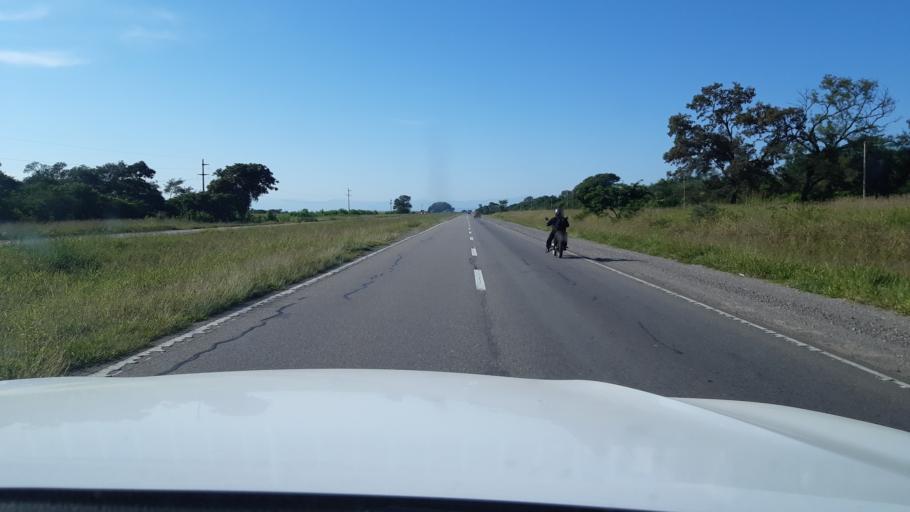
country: AR
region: Jujuy
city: Palpala
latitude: -24.3149
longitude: -65.1582
